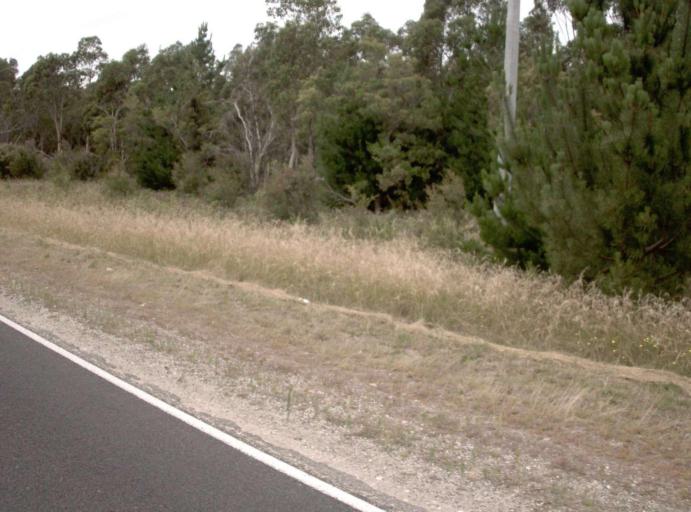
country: AU
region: Victoria
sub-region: Wellington
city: Sale
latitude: -38.1972
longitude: 147.2965
